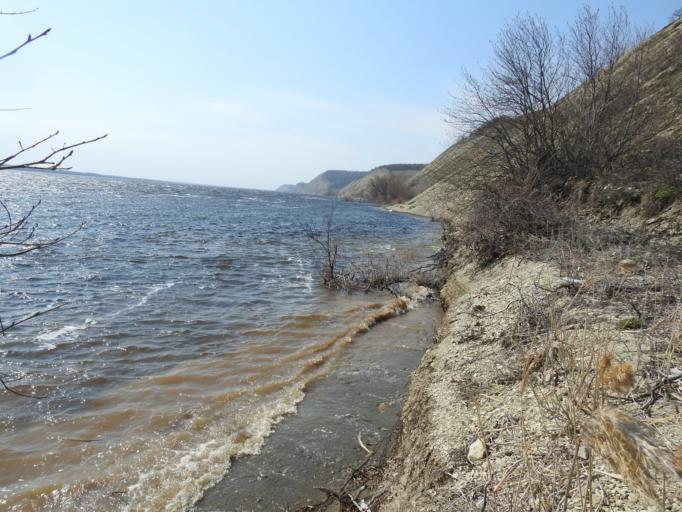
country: RU
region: Saratov
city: Voskresenskoye
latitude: 51.7917
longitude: 46.8563
